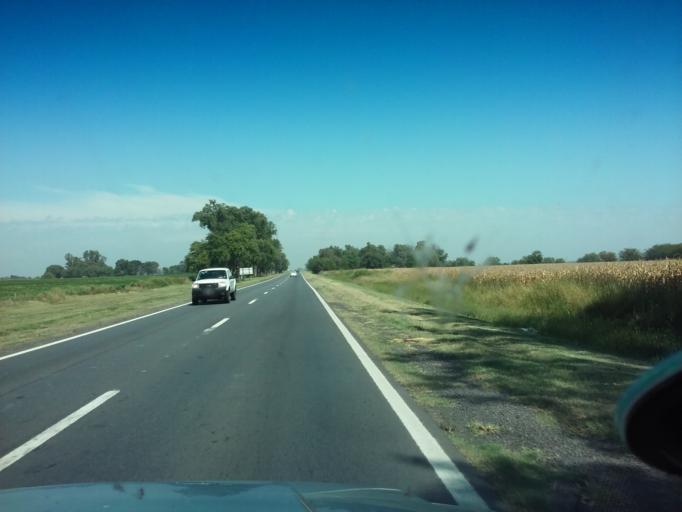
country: AR
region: Buenos Aires
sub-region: Partido de Nueve de Julio
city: Nueve de Julio
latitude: -35.4962
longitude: -60.9041
